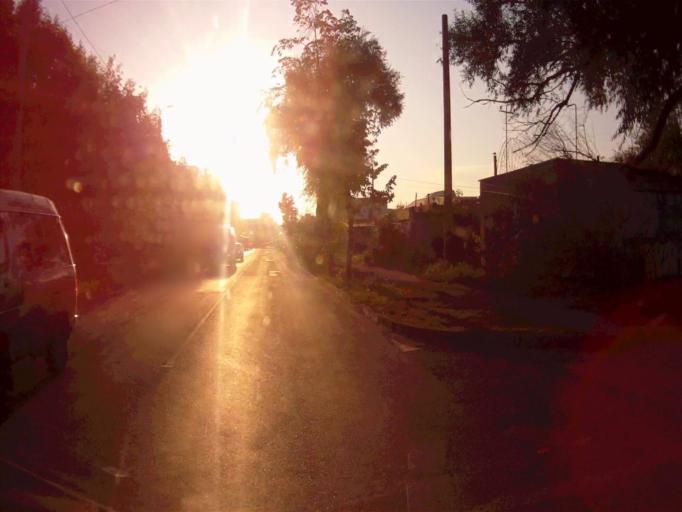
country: RU
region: Chelyabinsk
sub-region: Gorod Chelyabinsk
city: Chelyabinsk
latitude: 55.1624
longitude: 61.4378
